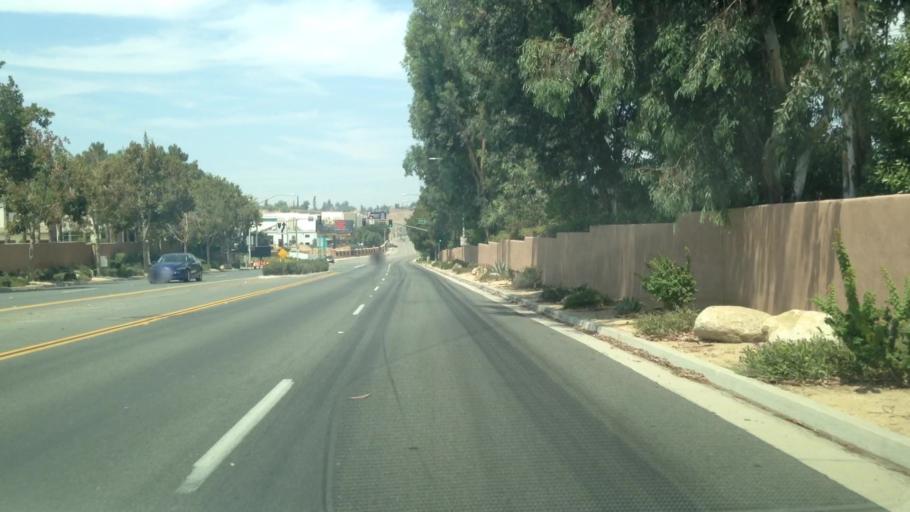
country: US
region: California
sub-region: Riverside County
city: El Cerrito
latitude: 33.7958
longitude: -117.5012
